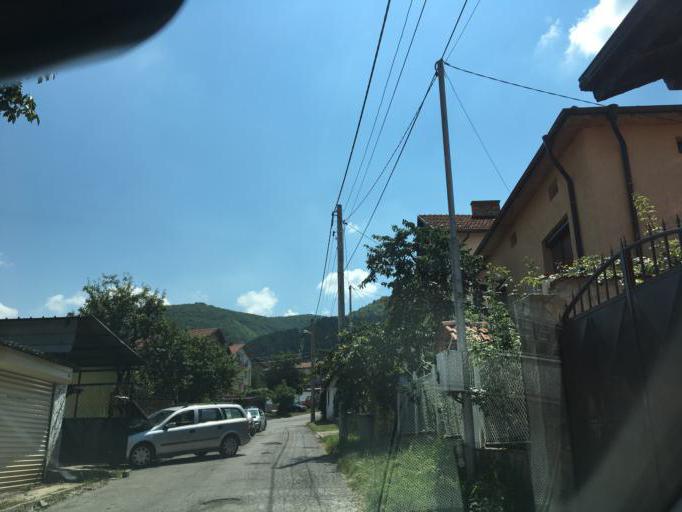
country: BG
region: Sofiya
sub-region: Obshtina Elin Pelin
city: Elin Pelin
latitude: 42.6031
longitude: 23.4721
